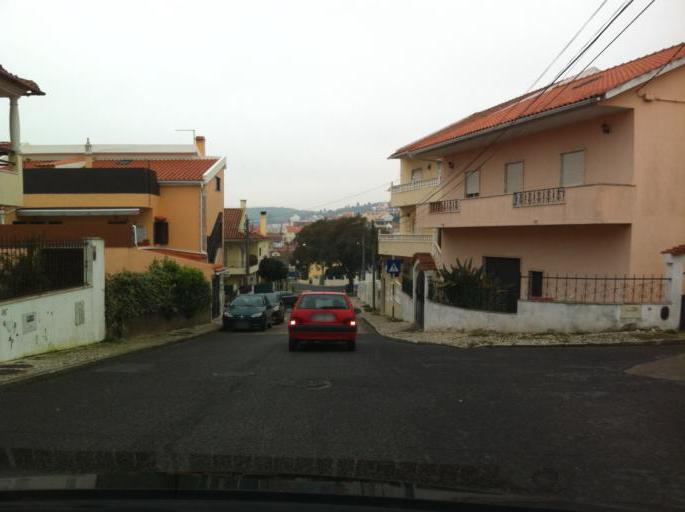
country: PT
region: Lisbon
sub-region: Odivelas
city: Famoes
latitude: 38.7866
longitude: -9.2208
